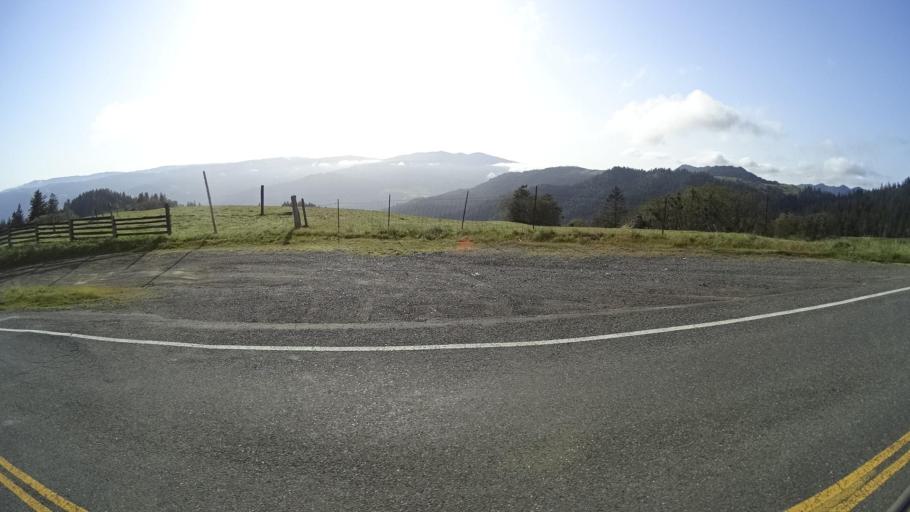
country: US
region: California
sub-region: Humboldt County
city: Blue Lake
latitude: 40.7367
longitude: -123.9453
